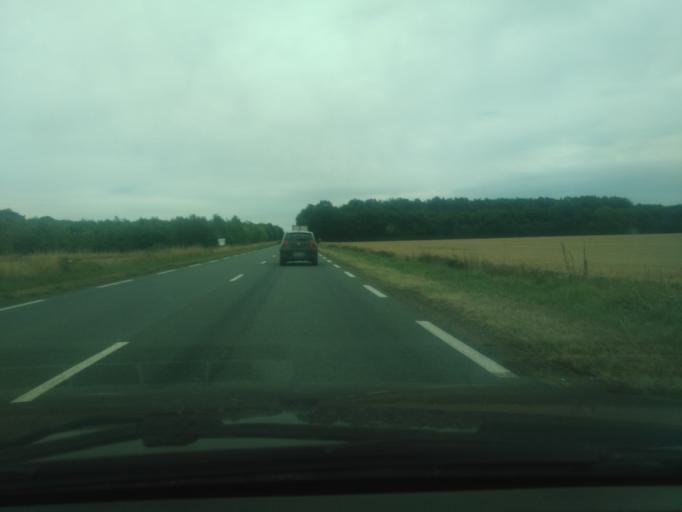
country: FR
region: Poitou-Charentes
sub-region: Departement de la Vienne
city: Chauvigny
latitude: 46.5749
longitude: 0.6874
